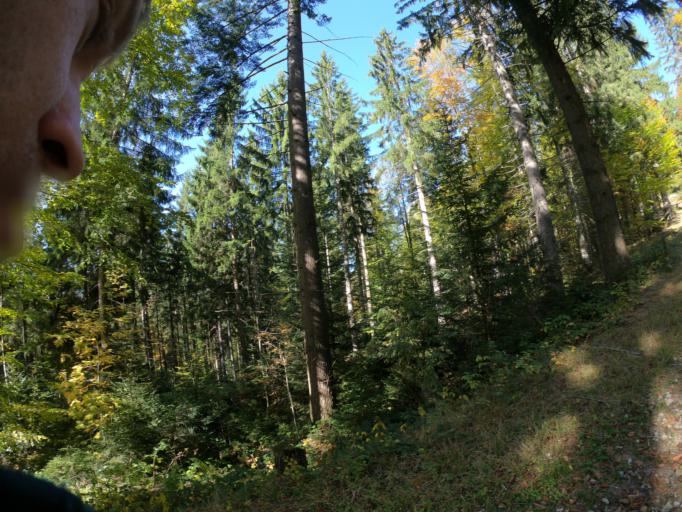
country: DE
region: Bavaria
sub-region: Lower Bavaria
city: Bodenmais
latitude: 49.0790
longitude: 13.1194
